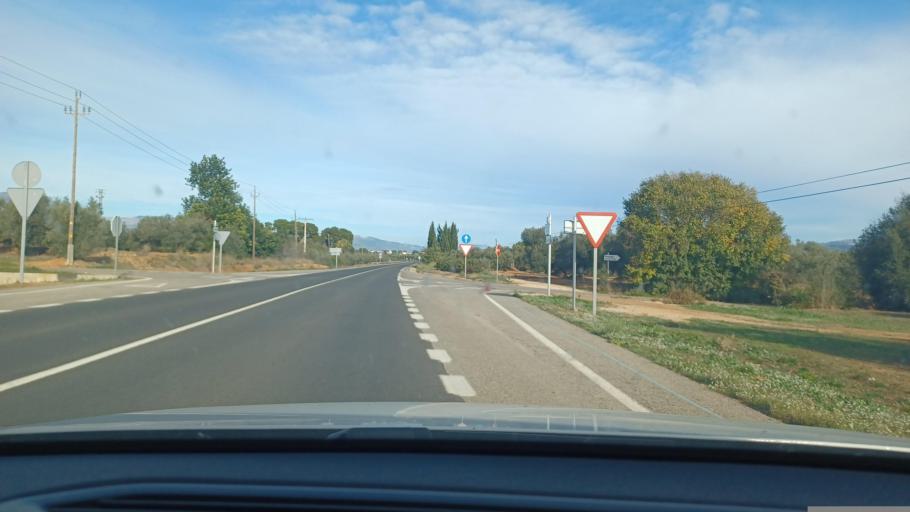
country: ES
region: Catalonia
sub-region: Provincia de Tarragona
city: Santa Barbara
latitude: 40.6901
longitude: 0.5069
